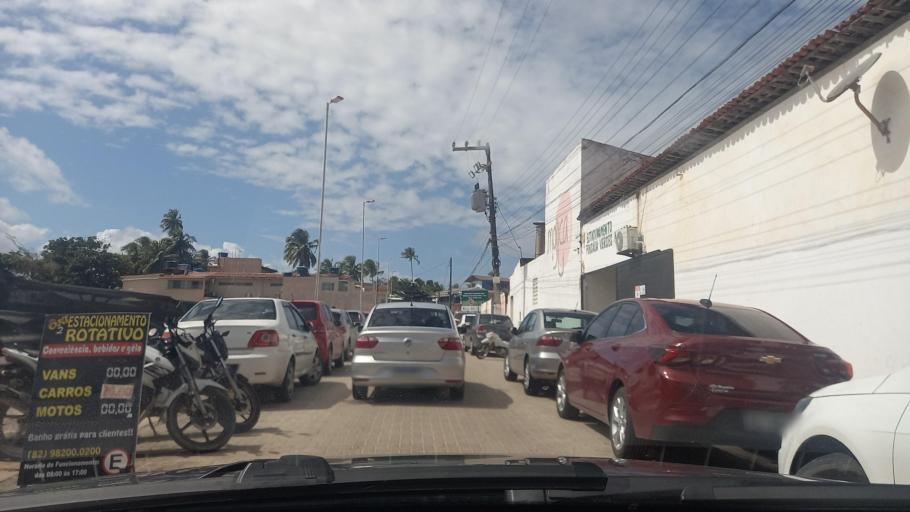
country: BR
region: Alagoas
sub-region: Marechal Deodoro
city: Marechal Deodoro
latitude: -9.7687
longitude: -35.8393
